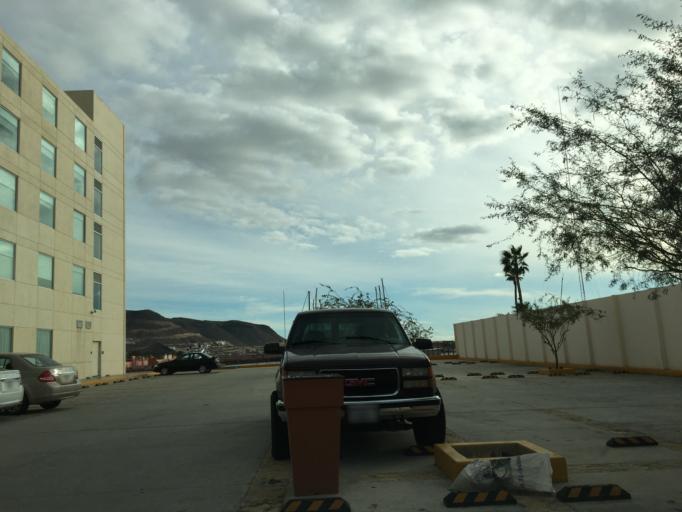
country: MX
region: Baja California Sur
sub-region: La Paz
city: La Paz
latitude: 24.2193
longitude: -110.3033
